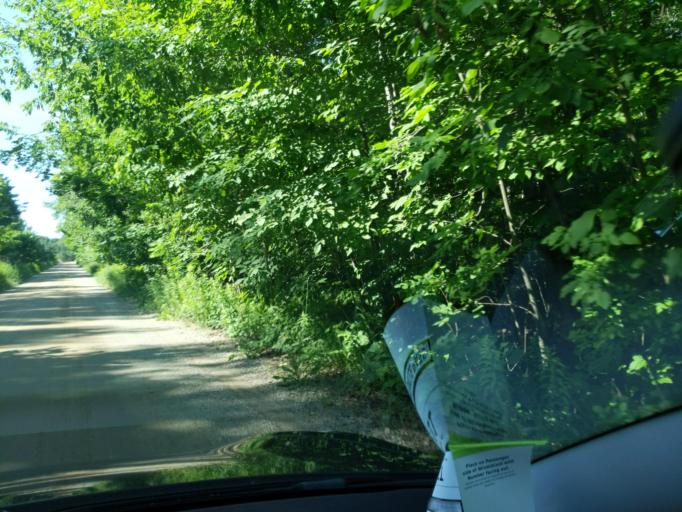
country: US
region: Michigan
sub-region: Mackinac County
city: Saint Ignace
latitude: 45.6829
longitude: -84.7126
